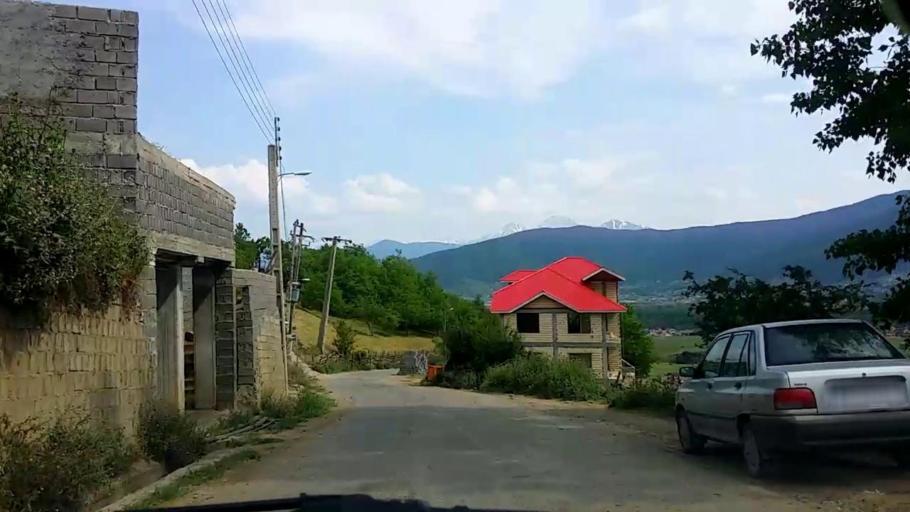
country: IR
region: Mazandaran
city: `Abbasabad
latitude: 36.5534
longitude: 51.1814
